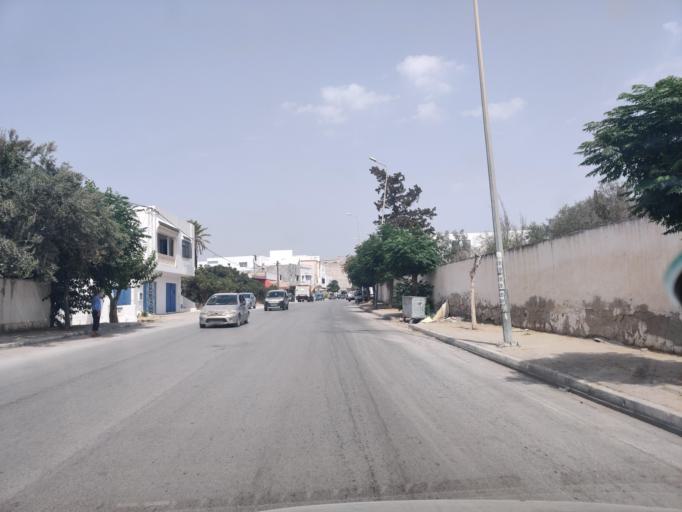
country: TN
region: Nabul
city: Al Hammamat
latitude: 36.4113
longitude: 10.5997
